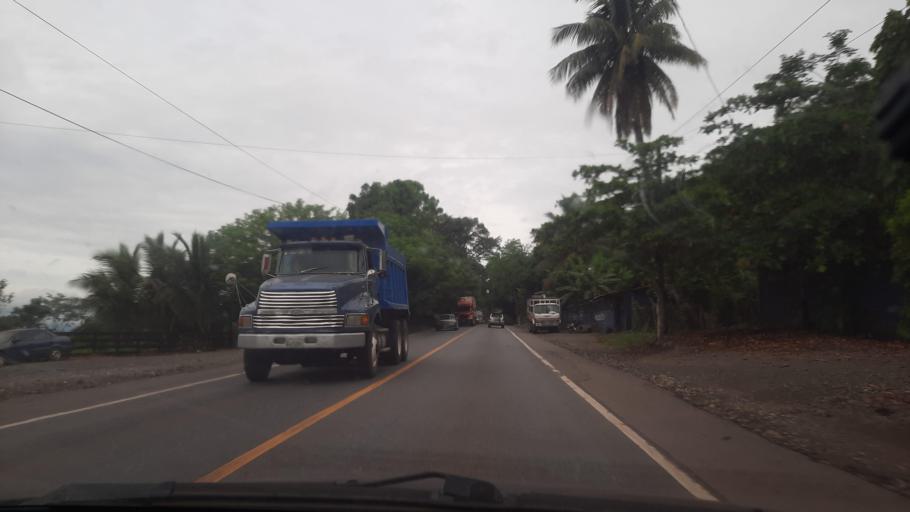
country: GT
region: Izabal
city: Morales
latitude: 15.4318
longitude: -88.9685
